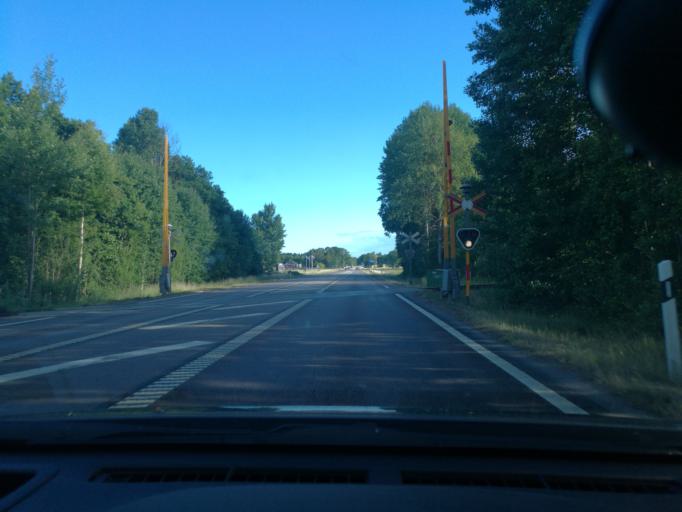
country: SE
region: Kalmar
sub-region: Monsteras Kommun
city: Moensteras
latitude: 57.0312
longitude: 16.4326
